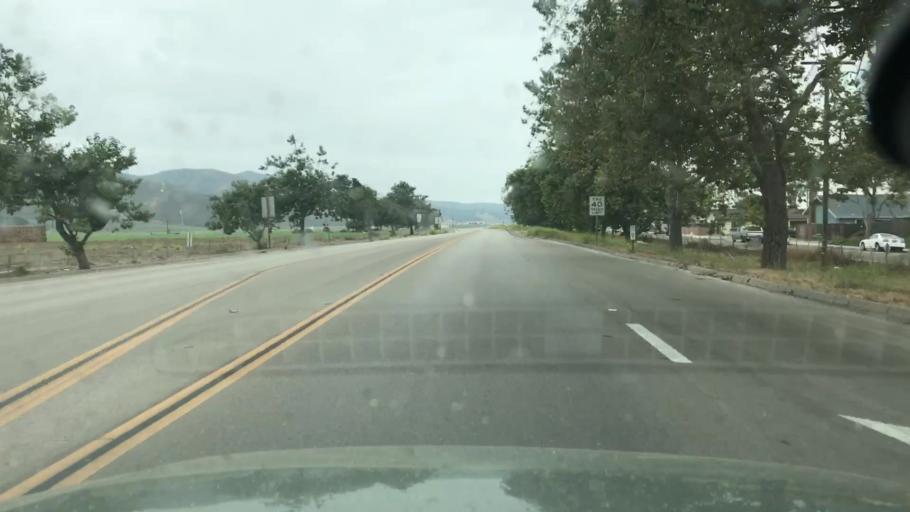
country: US
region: California
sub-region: Santa Barbara County
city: Lompoc
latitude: 34.6391
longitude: -120.4757
